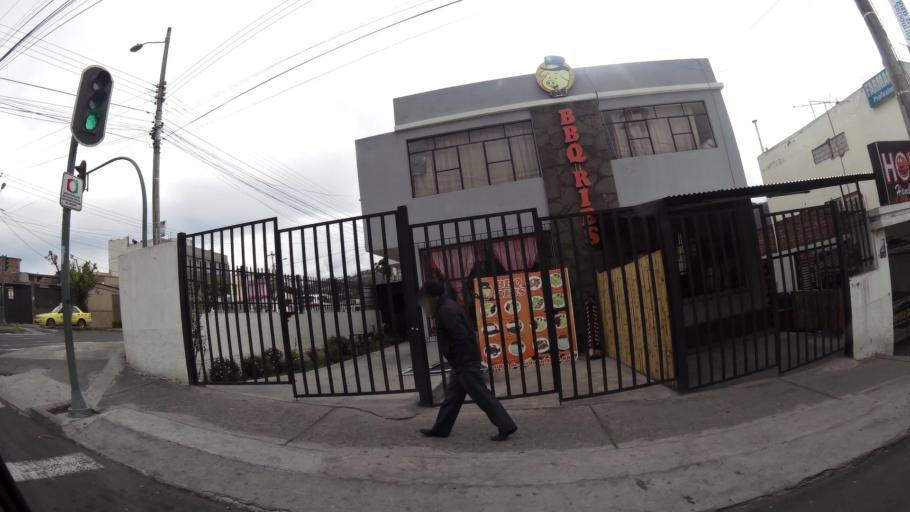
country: EC
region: Tungurahua
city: Ambato
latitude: -1.2532
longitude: -78.6297
